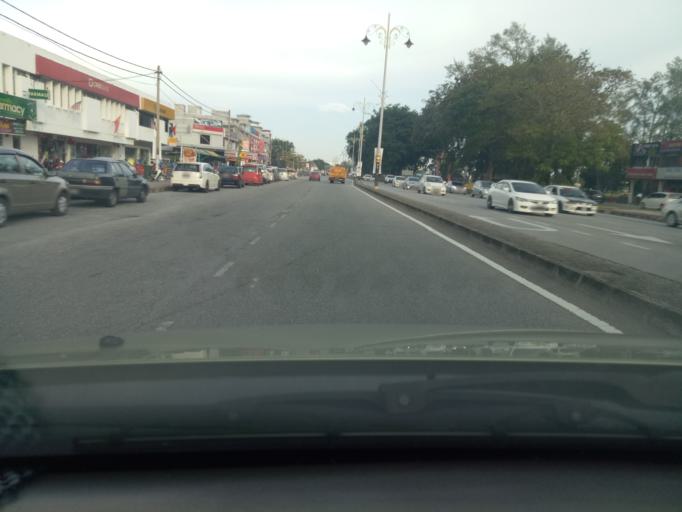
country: MY
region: Kedah
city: Alor Setar
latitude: 6.1284
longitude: 100.3503
